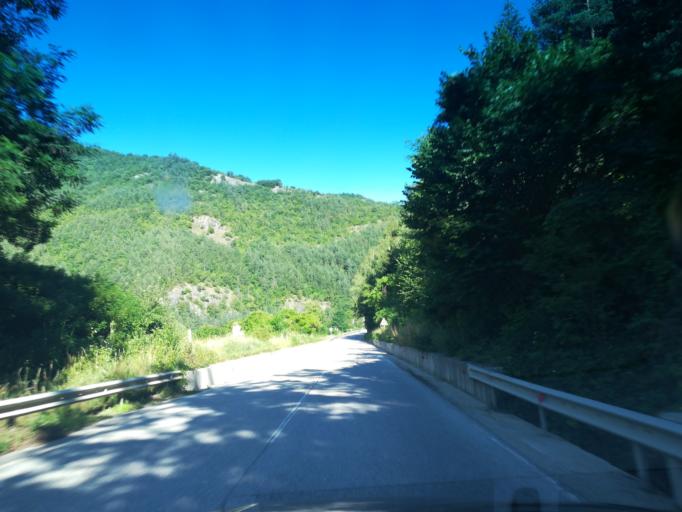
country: BG
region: Smolyan
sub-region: Obshtina Chepelare
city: Chepelare
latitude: 41.8264
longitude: 24.6891
